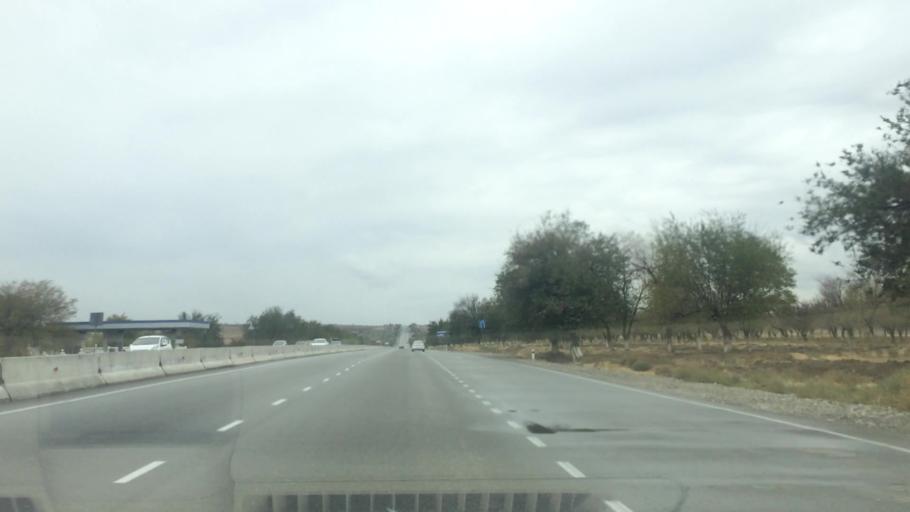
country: UZ
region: Samarqand
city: Bulung'ur
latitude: 39.8812
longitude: 67.4860
